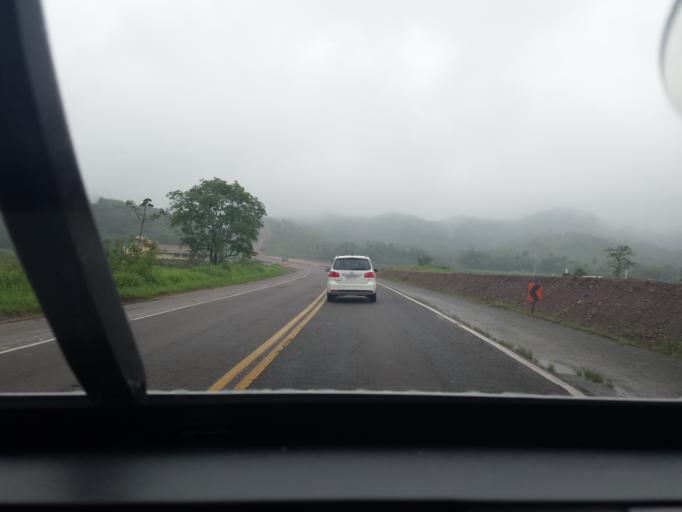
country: BR
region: Santa Catarina
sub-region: Itajai
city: Itajai
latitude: -26.8349
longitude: -48.7561
